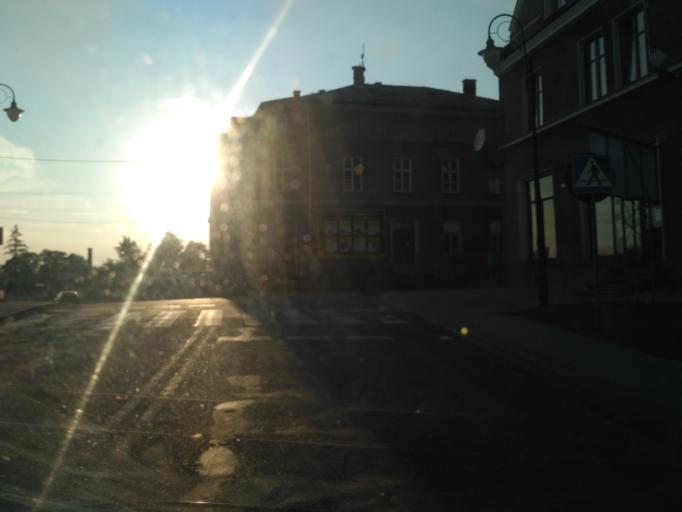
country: PL
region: Subcarpathian Voivodeship
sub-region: Powiat krosnienski
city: Korczyna
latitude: 49.7153
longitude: 21.8098
